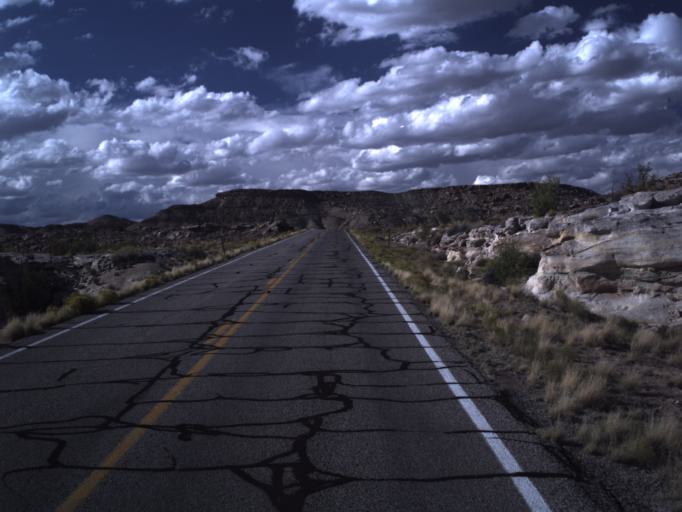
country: US
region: Utah
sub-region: San Juan County
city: Blanding
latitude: 37.3119
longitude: -109.3035
